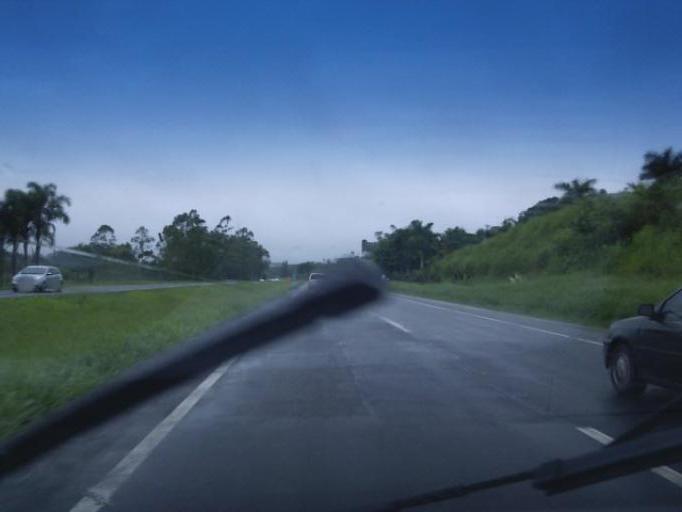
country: BR
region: Sao Paulo
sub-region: Registro
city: Registro
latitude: -24.4200
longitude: -47.7696
